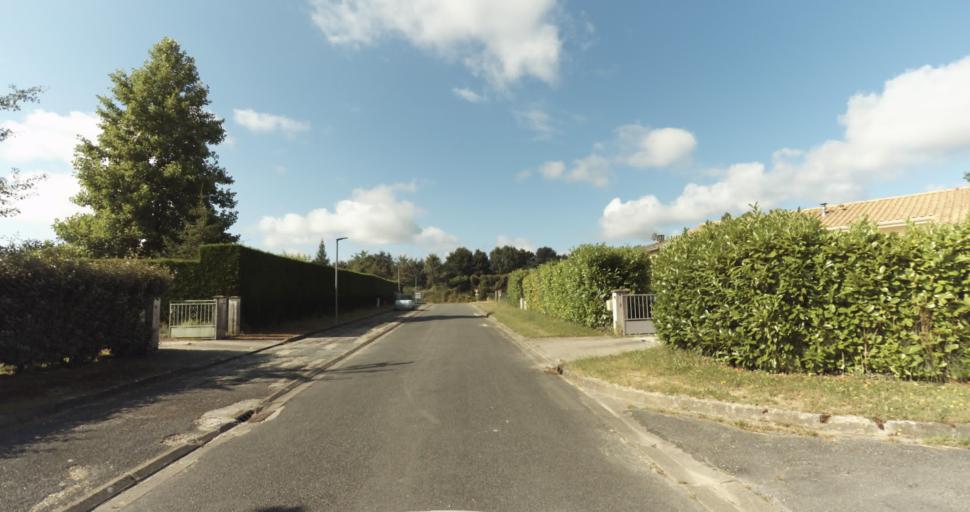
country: FR
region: Aquitaine
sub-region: Departement de la Gironde
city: Bazas
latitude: 44.4268
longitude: -0.2118
